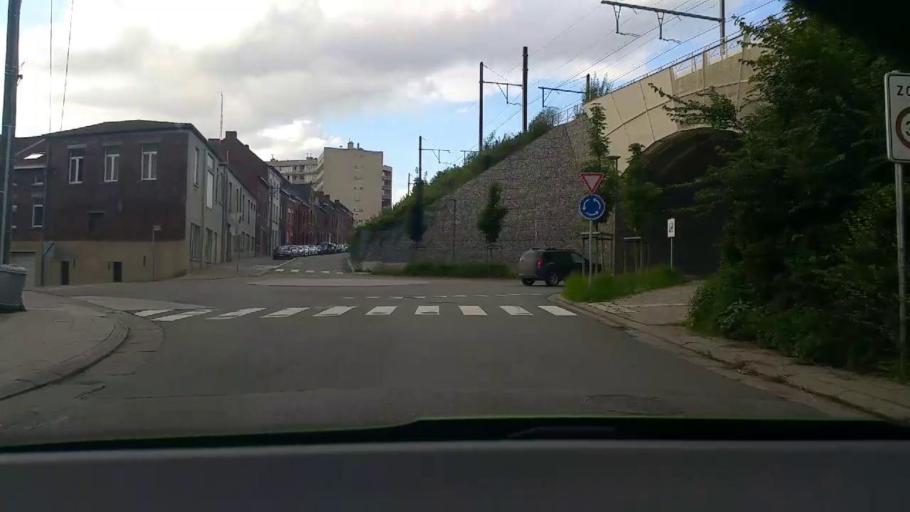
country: BE
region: Wallonia
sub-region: Province du Brabant Wallon
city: Nivelles
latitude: 50.5967
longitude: 4.3358
